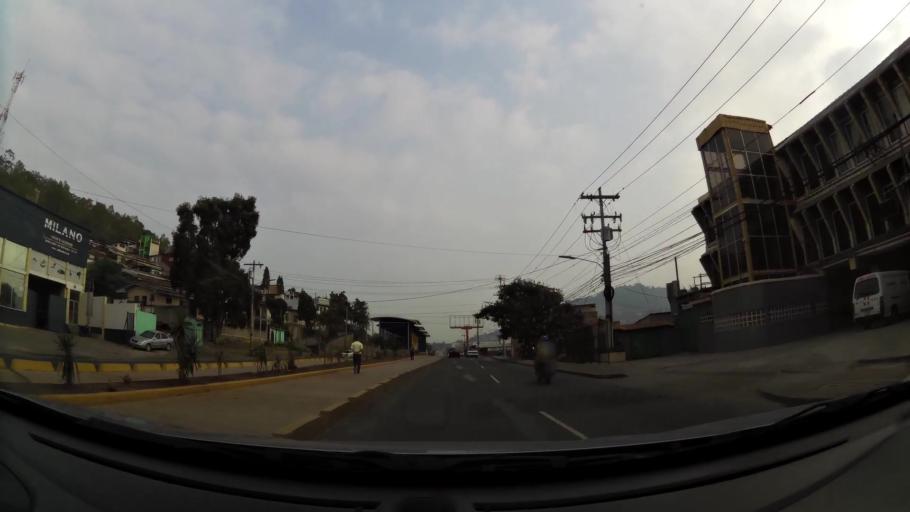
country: HN
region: Francisco Morazan
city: Tegucigalpa
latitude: 14.0927
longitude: -87.1977
